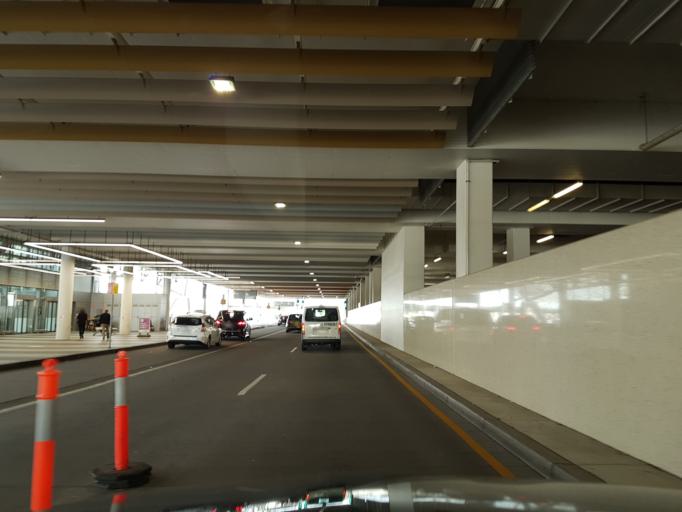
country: AU
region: South Australia
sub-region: City of West Torrens
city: Plympton
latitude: -34.9374
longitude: 138.5370
